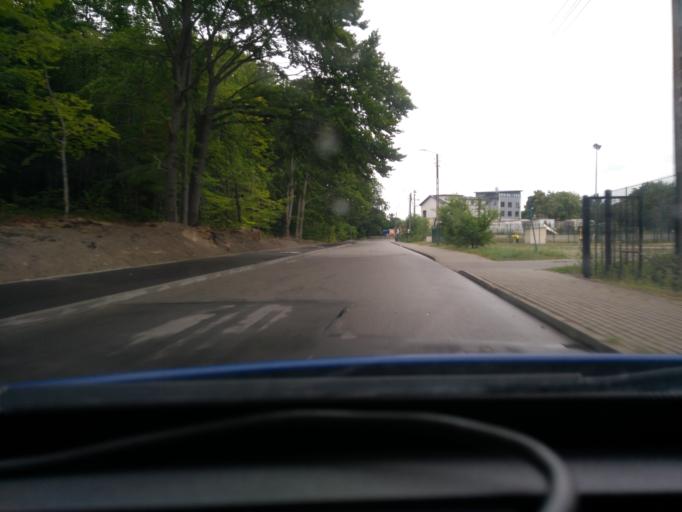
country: PL
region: Pomeranian Voivodeship
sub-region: Powiat kartuski
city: Kartuzy
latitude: 54.3410
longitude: 18.2081
